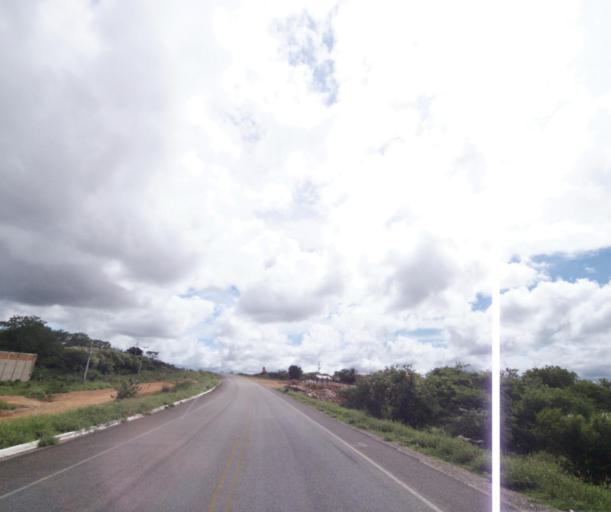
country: BR
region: Bahia
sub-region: Brumado
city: Brumado
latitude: -14.2310
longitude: -41.6798
